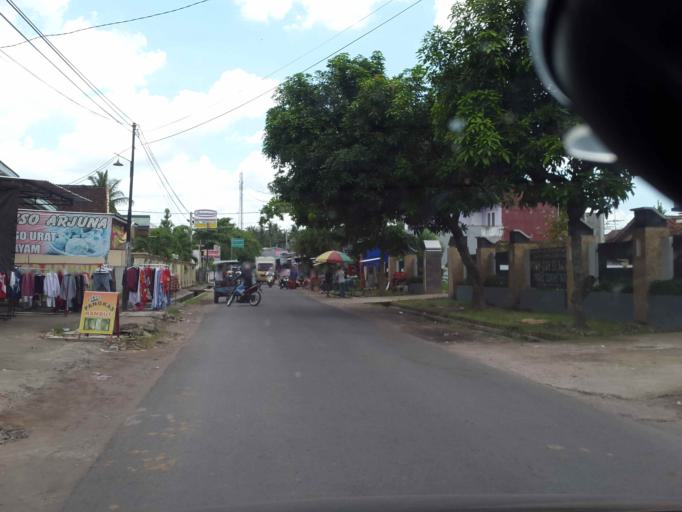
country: ID
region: West Nusa Tenggara
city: Mambalan
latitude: -8.5428
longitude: 116.1053
